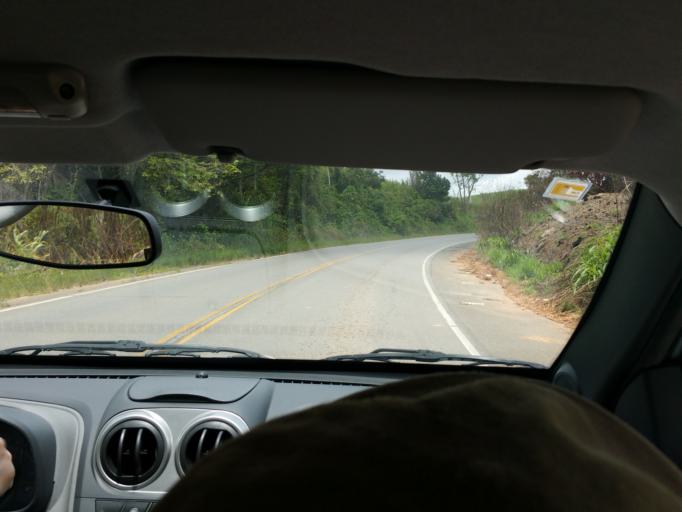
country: BR
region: Pernambuco
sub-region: Sirinhaem
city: Sirinhaem
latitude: -8.6207
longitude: -35.1263
